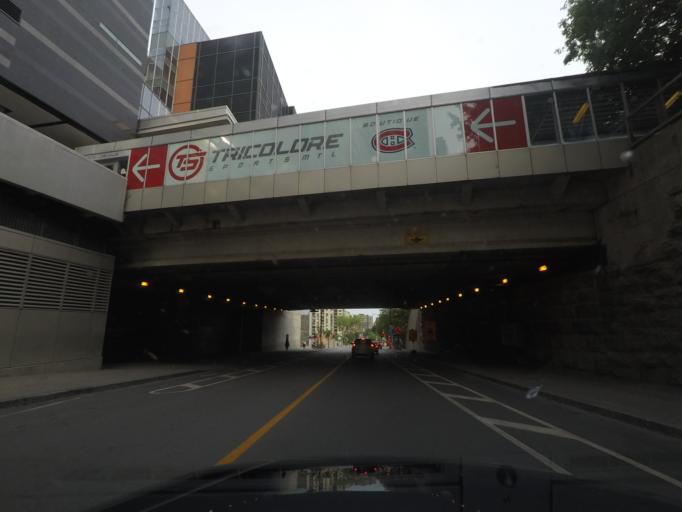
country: CA
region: Quebec
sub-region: Montreal
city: Montreal
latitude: 45.4955
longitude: -73.5702
